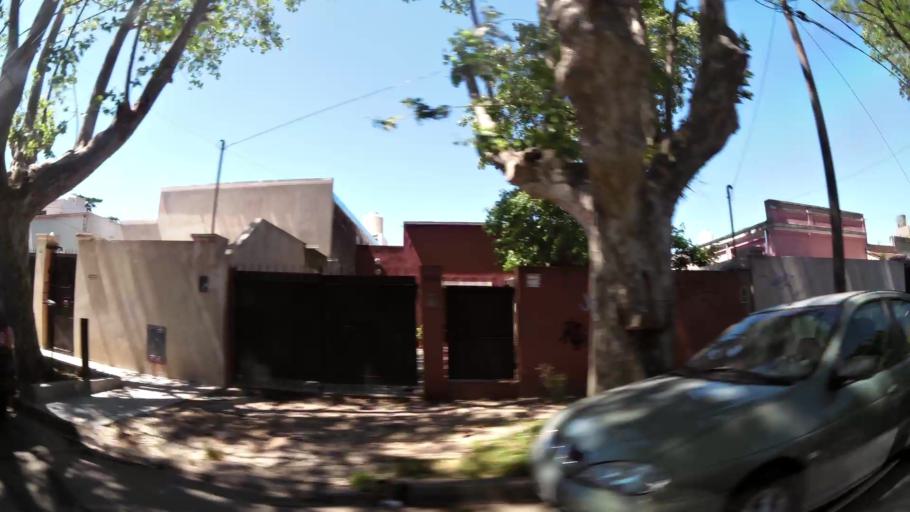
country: AR
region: Buenos Aires
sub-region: Partido de San Isidro
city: San Isidro
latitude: -34.4715
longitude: -58.5253
